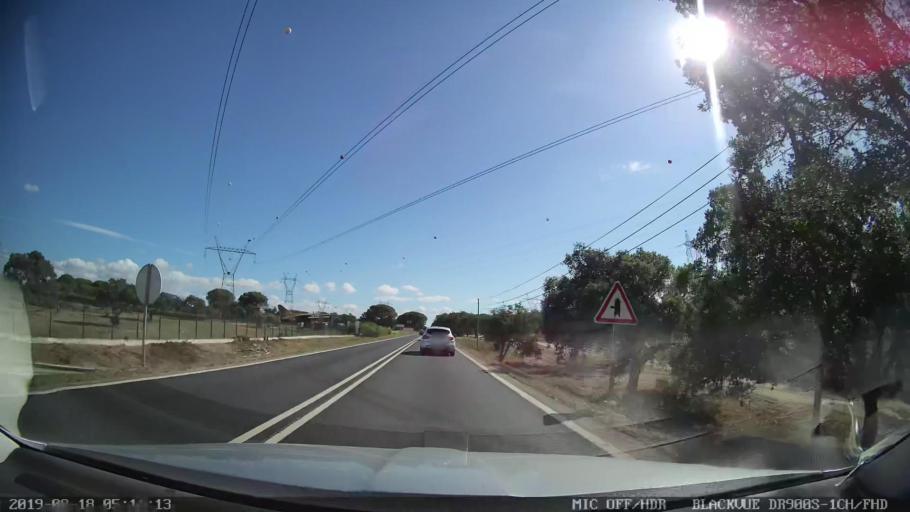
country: PT
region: Setubal
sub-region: Alcochete
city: Alcochete
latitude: 38.7765
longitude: -8.8858
